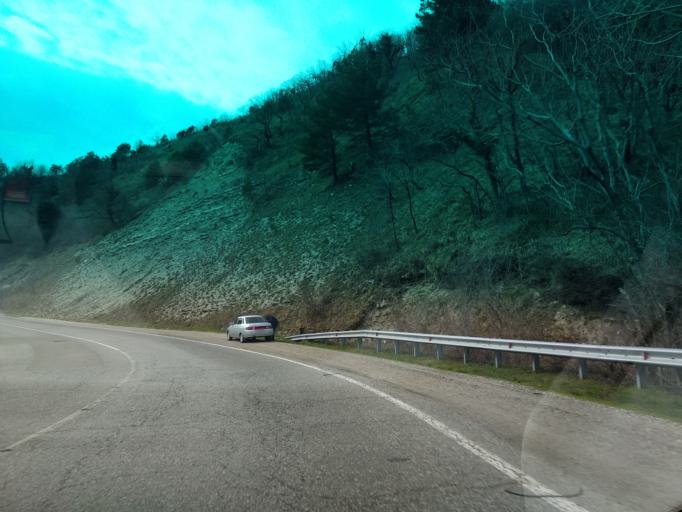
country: RU
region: Krasnodarskiy
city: Tuapse
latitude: 44.0889
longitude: 39.1295
